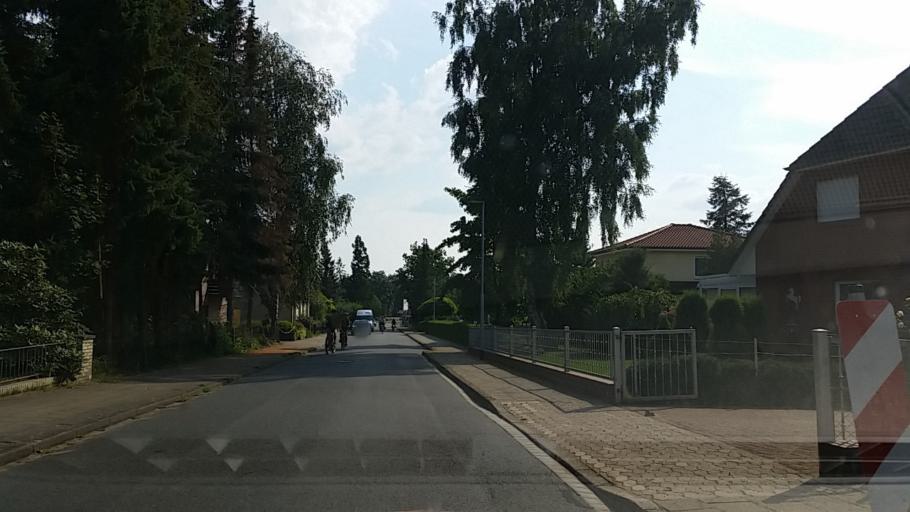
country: DE
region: Lower Saxony
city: Schneverdingen
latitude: 53.1219
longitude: 9.7947
